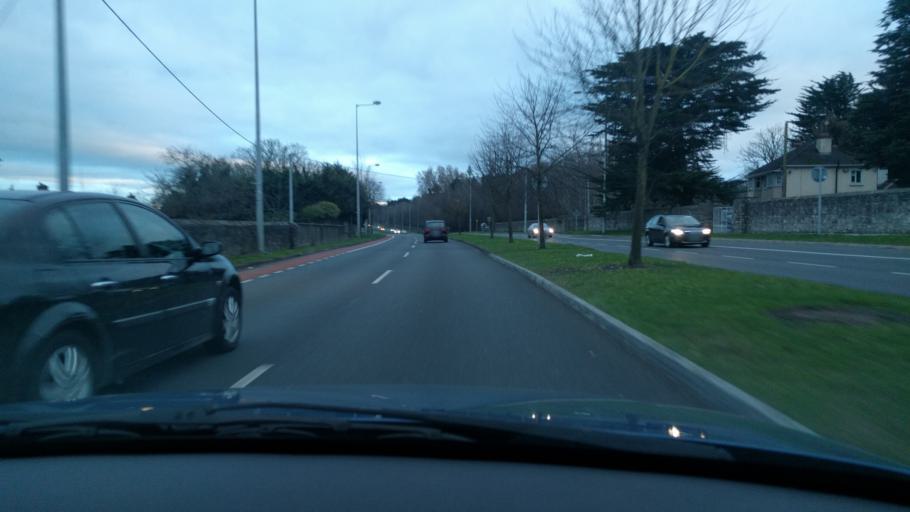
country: IE
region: Leinster
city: Clondalkin
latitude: 53.3102
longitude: -6.3883
